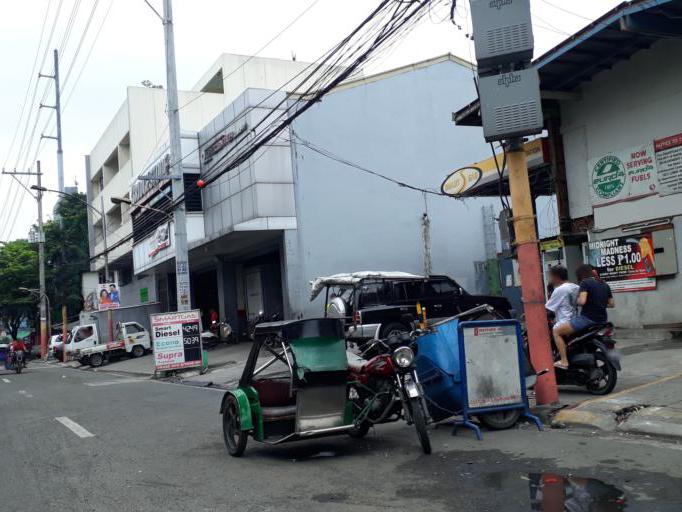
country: PH
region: Metro Manila
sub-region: City of Manila
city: Manila
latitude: 14.6256
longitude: 120.9785
